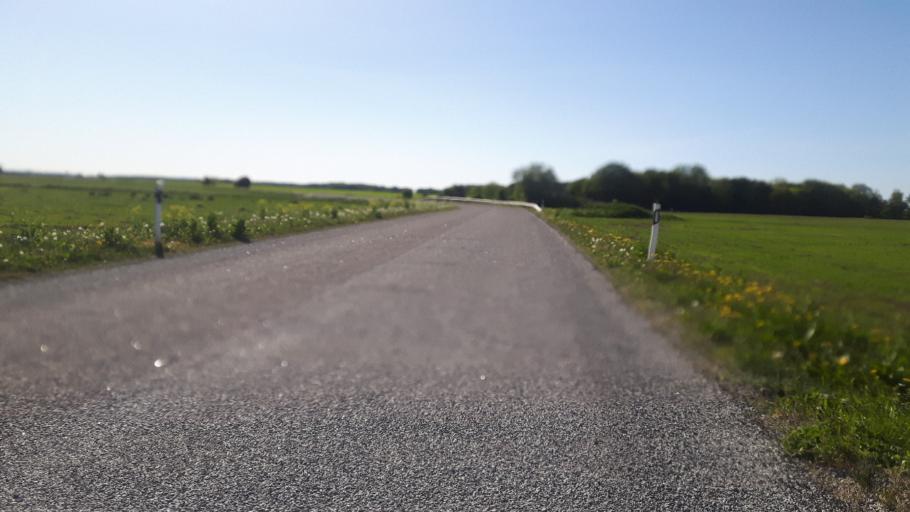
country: EE
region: Ida-Virumaa
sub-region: Kohtla-Jaerve linn
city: Kohtla-Jarve
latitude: 59.4401
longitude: 27.2746
